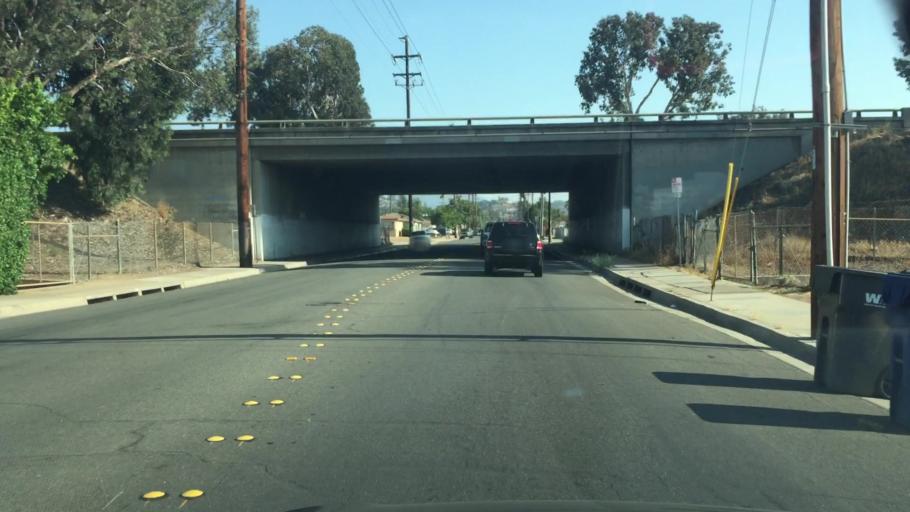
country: US
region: California
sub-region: San Diego County
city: Bostonia
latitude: 32.8037
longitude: -116.9446
